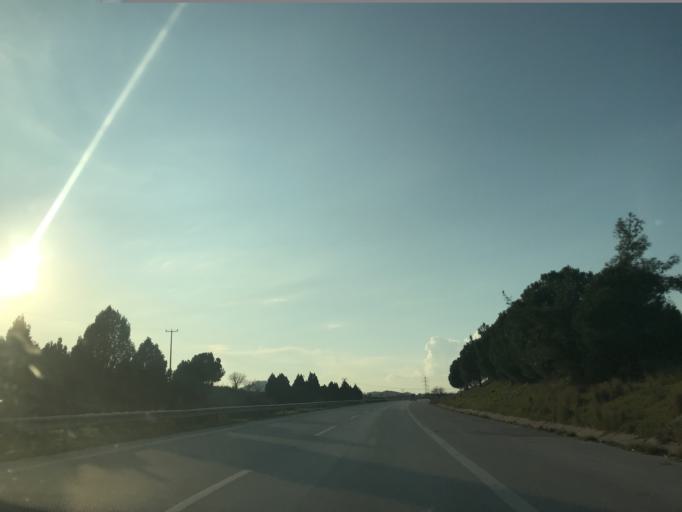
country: TR
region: Osmaniye
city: Toprakkale
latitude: 36.9673
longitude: 36.0391
